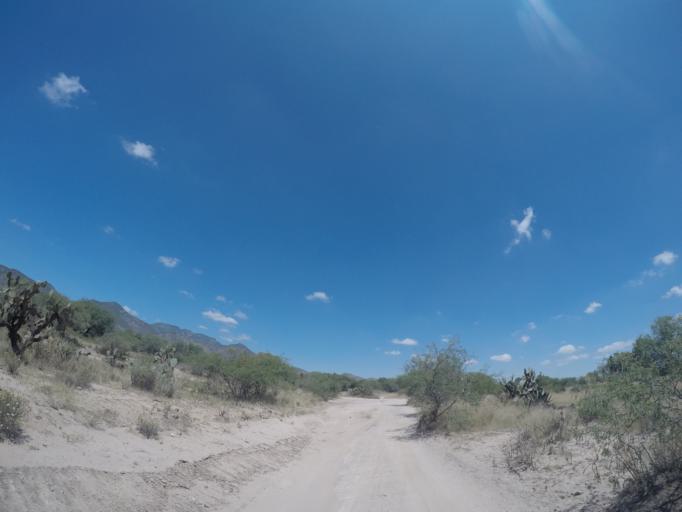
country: MX
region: San Luis Potosi
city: La Pila
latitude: 21.9883
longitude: -100.8991
